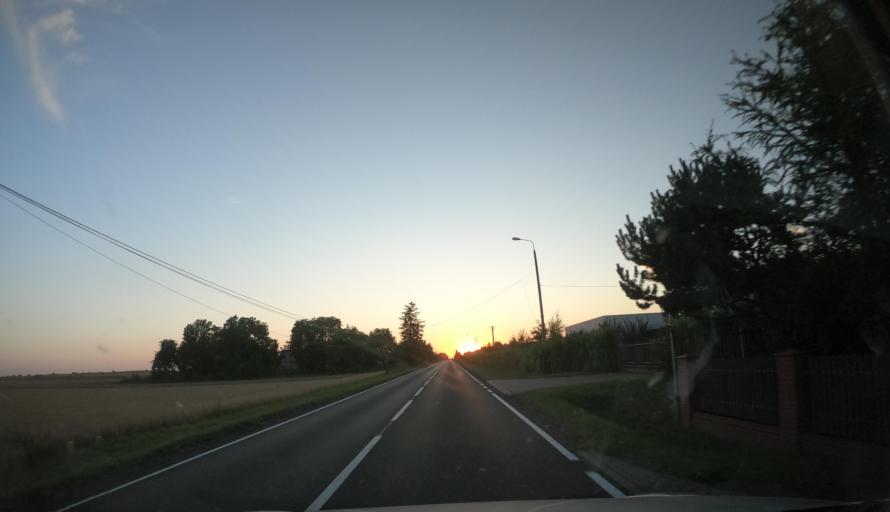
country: PL
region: Kujawsko-Pomorskie
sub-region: Powiat bydgoski
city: Koronowo
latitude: 53.3415
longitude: 17.8730
